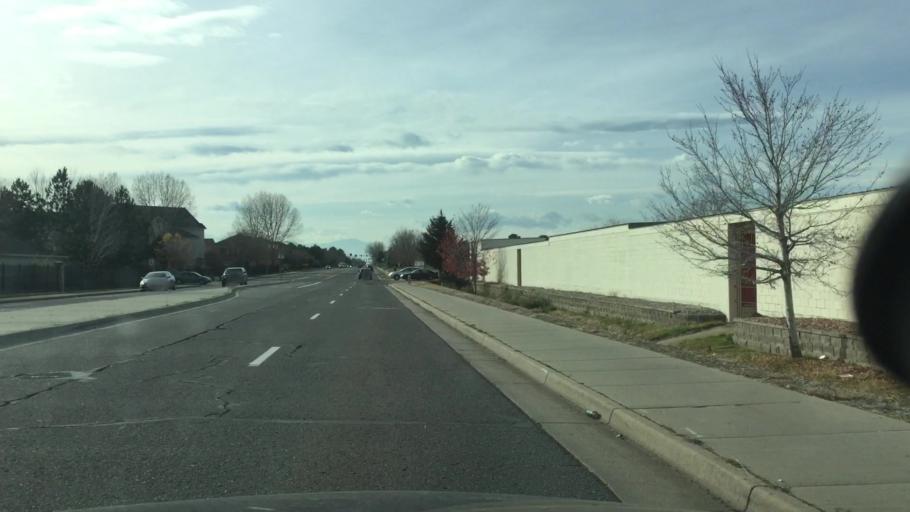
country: US
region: Colorado
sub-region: Arapahoe County
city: Glendale
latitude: 39.6894
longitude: -104.8764
